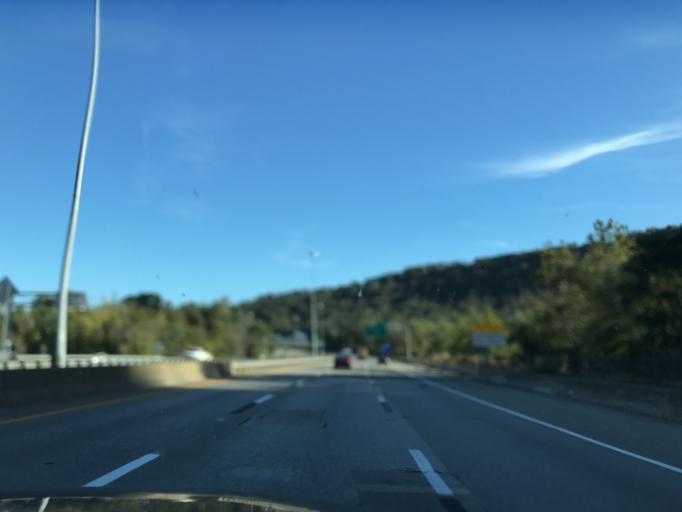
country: US
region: West Virginia
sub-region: Ohio County
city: Wheeling
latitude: 40.0716
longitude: -80.6991
